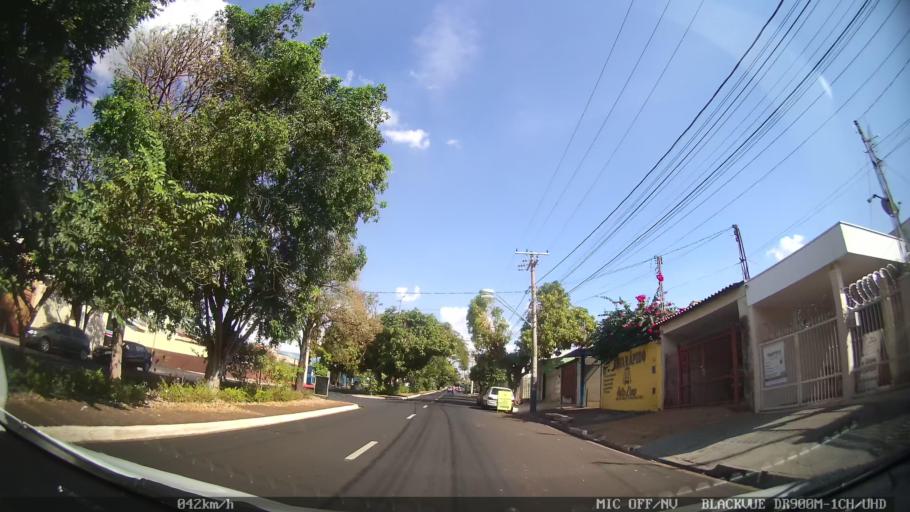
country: BR
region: Sao Paulo
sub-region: Ribeirao Preto
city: Ribeirao Preto
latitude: -21.1824
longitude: -47.8327
